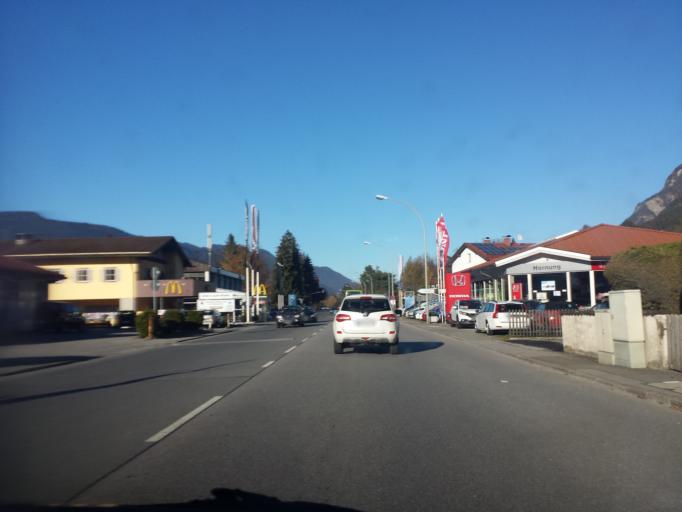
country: DE
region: Bavaria
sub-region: Upper Bavaria
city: Garmisch-Partenkirchen
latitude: 47.5016
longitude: 11.1021
